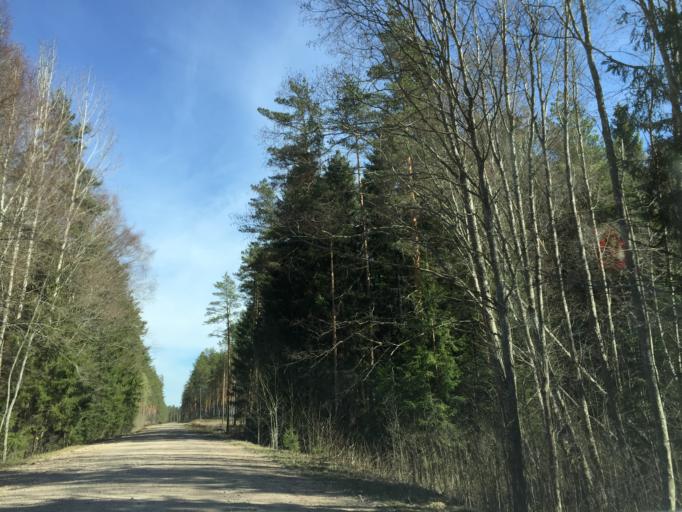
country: LV
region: Strenci
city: Seda
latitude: 57.6251
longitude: 25.8473
